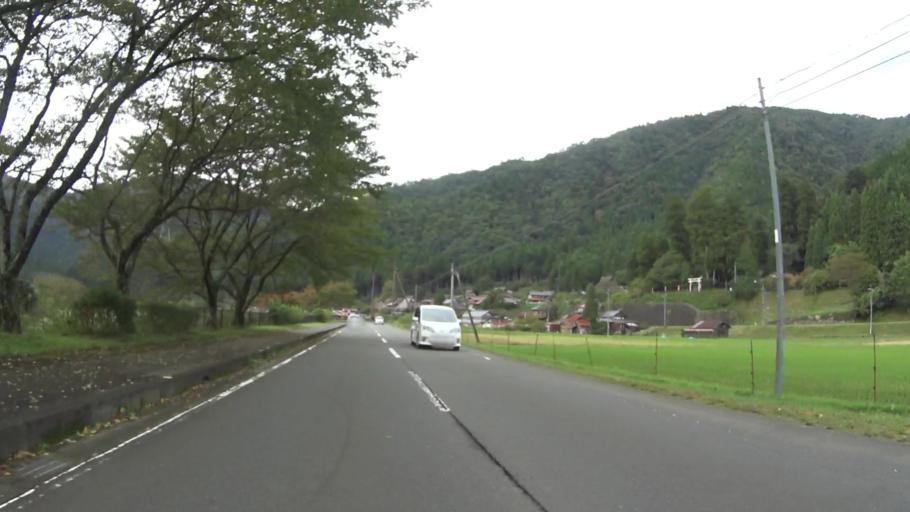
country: JP
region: Fukui
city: Obama
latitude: 35.3110
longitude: 135.6264
